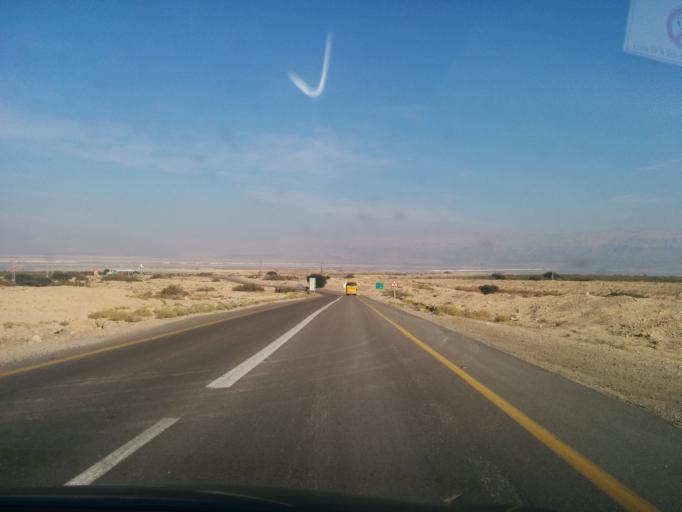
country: IL
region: Southern District
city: `En Boqeq
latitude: 31.1435
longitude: 35.3644
